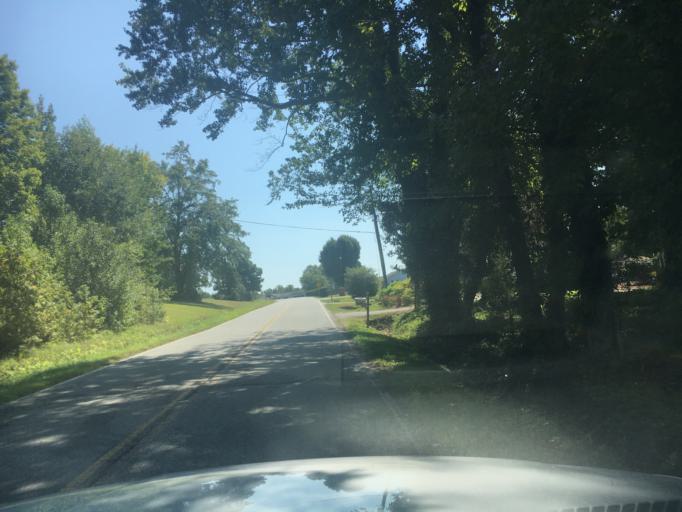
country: US
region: South Carolina
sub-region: Spartanburg County
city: Inman
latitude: 35.1209
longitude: -82.0392
